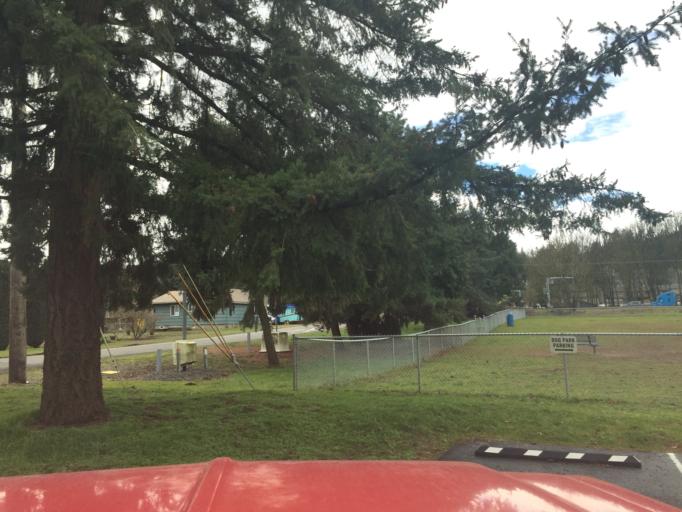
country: US
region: Oregon
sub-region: Columbia County
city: Columbia City
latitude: 45.8939
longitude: -122.8105
